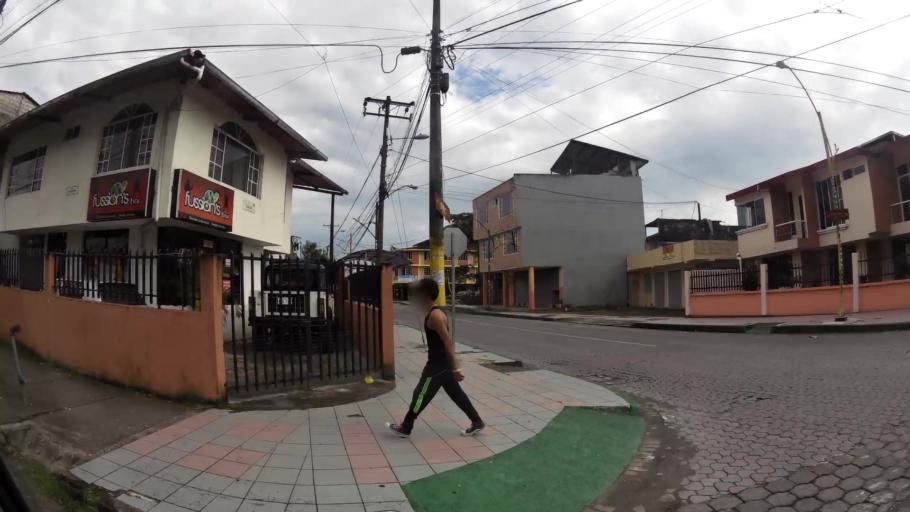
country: EC
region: Pastaza
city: Puyo
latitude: -1.4832
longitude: -77.9984
